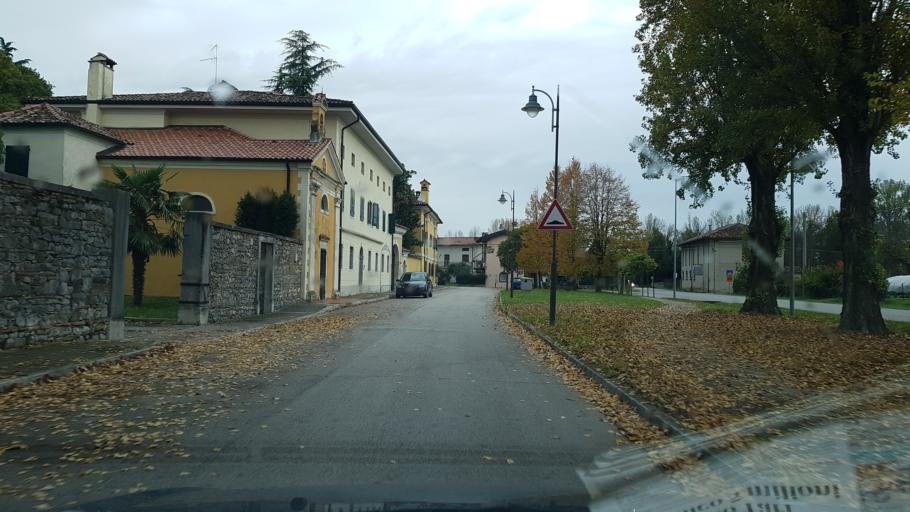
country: IT
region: Friuli Venezia Giulia
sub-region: Provincia di Udine
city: Fiumicello
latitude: 45.7994
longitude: 13.4037
